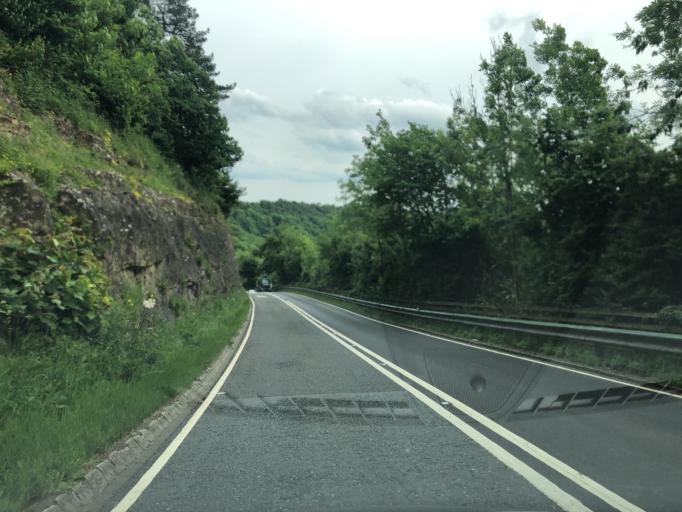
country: GB
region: England
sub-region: North Yorkshire
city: Angram Grange
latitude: 54.2396
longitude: -1.2123
